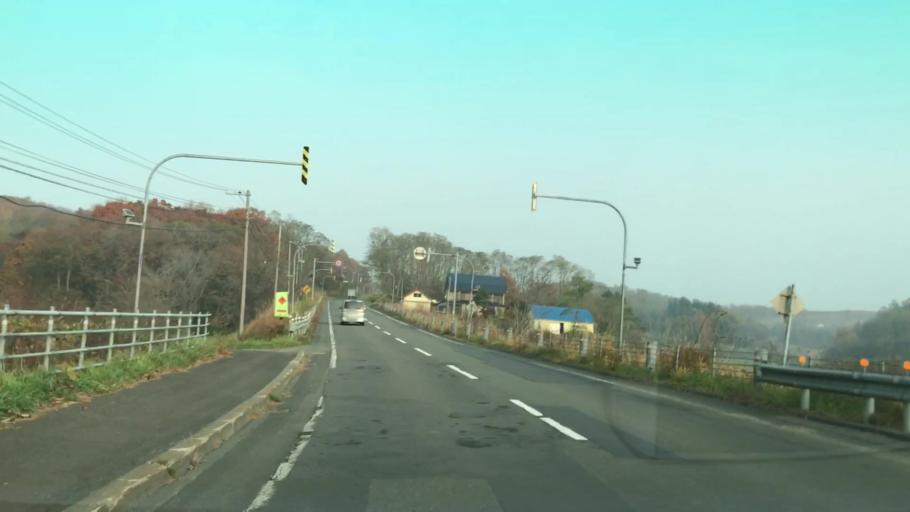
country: JP
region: Hokkaido
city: Ishikari
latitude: 43.3248
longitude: 141.4433
